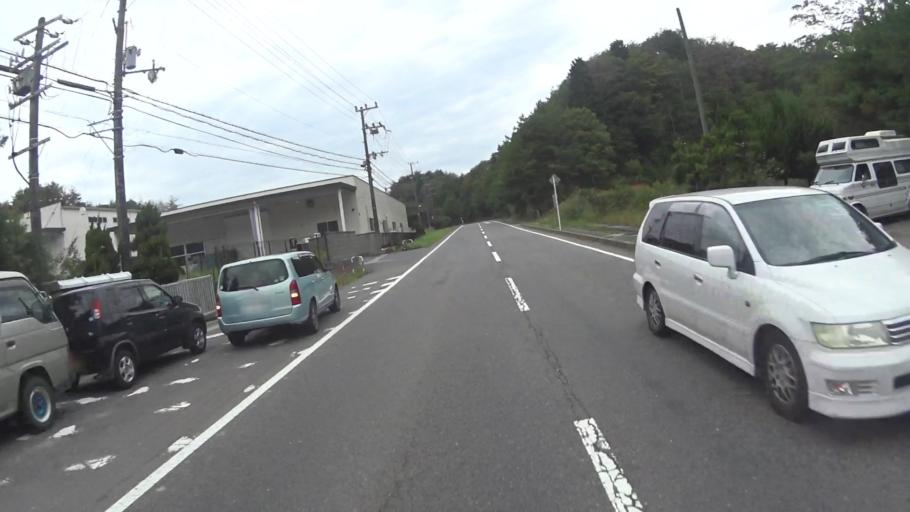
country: JP
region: Mie
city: Ueno-ebisumachi
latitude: 34.8553
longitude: 136.0138
